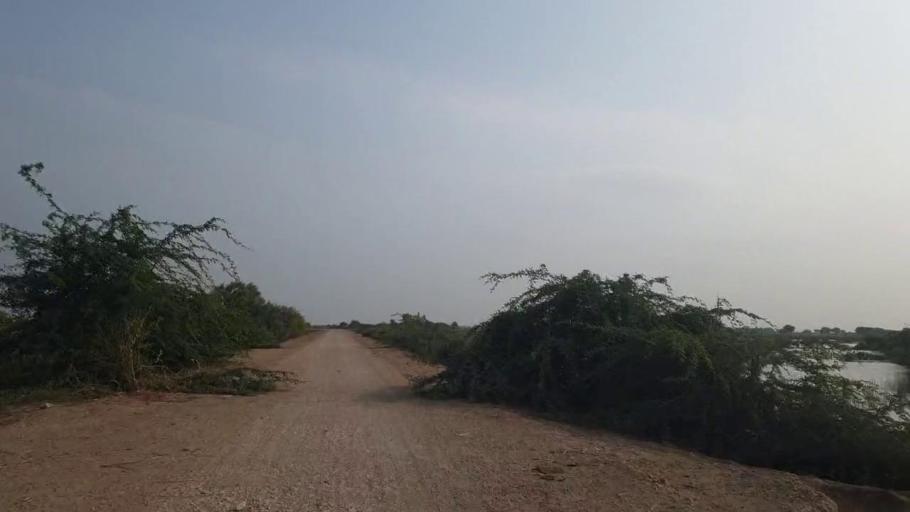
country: PK
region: Sindh
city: Badin
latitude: 24.6024
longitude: 68.6961
